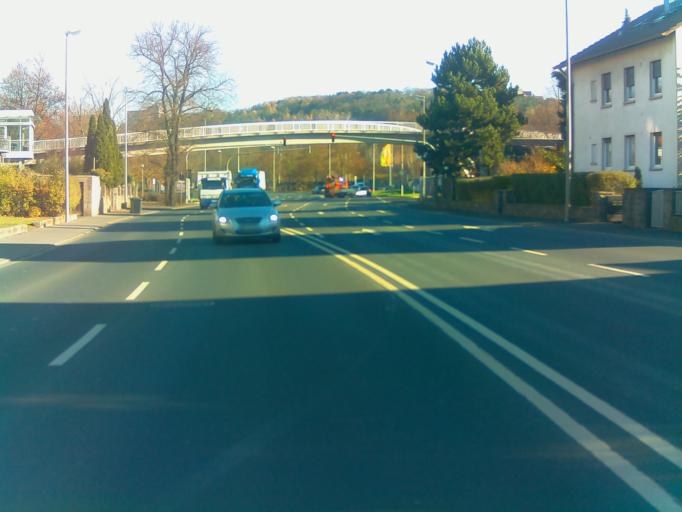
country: DE
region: Bavaria
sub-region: Regierungsbezirk Unterfranken
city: Bad Neustadt an der Saale
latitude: 50.3206
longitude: 10.2149
